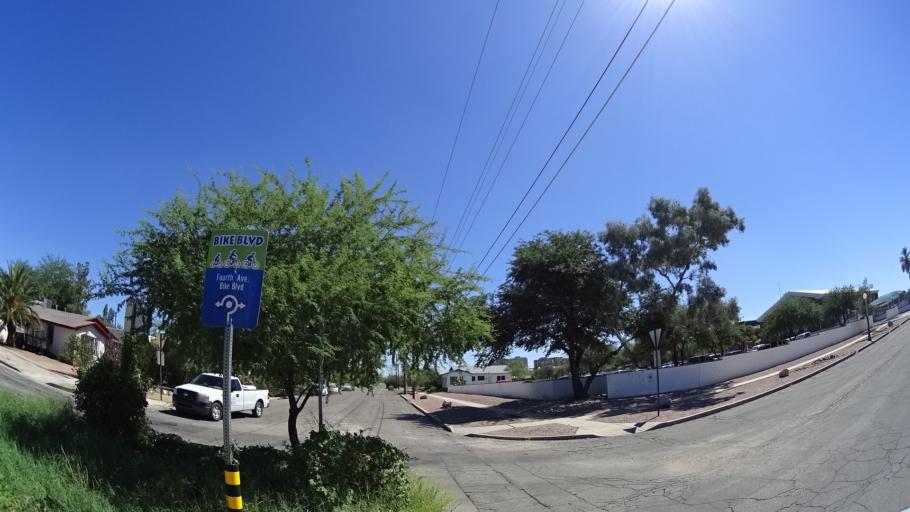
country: US
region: Arizona
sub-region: Pima County
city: South Tucson
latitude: 32.2372
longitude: -110.9657
